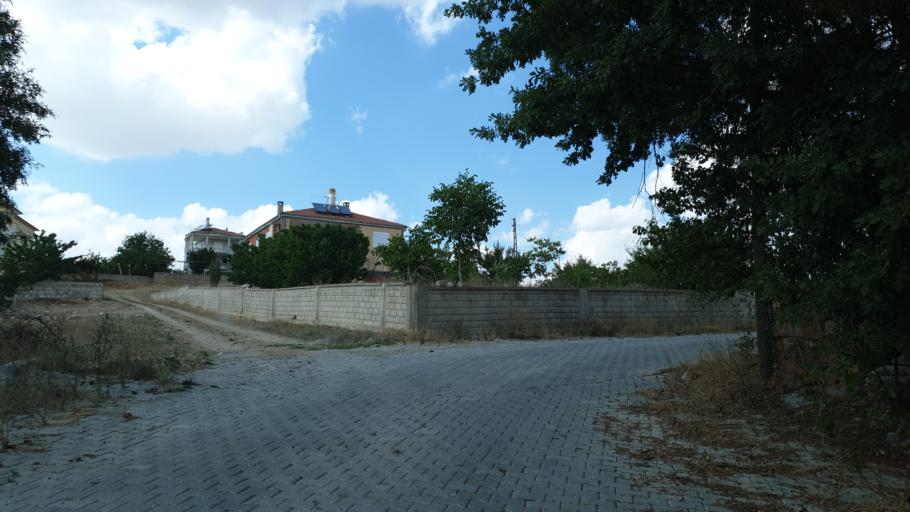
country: TR
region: Kayseri
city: Felahiye
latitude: 39.1156
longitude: 35.6085
